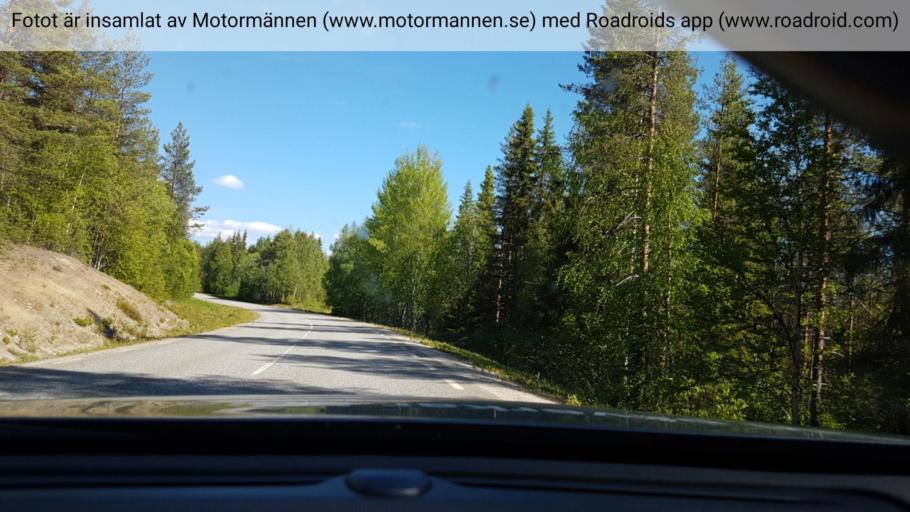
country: SE
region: Vaesterbotten
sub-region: Lycksele Kommun
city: Soderfors
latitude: 64.6207
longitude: 18.2752
